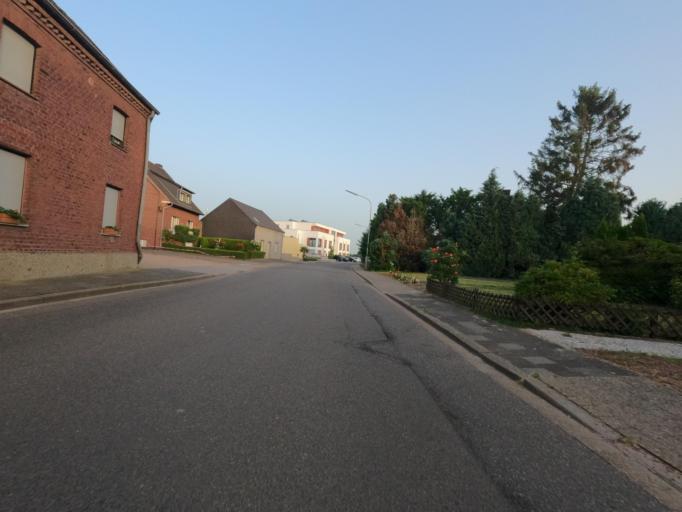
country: DE
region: North Rhine-Westphalia
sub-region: Regierungsbezirk Koln
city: Heinsberg
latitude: 51.0688
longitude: 6.1285
